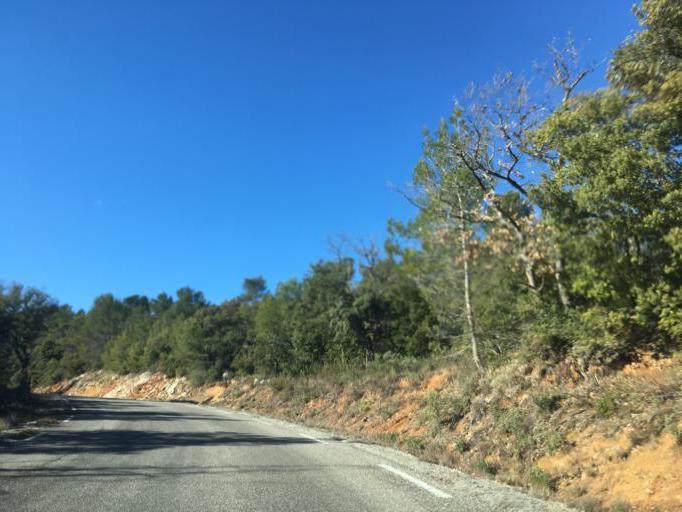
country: FR
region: Provence-Alpes-Cote d'Azur
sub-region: Departement du Var
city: Barjols
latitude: 43.5934
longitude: 6.0750
